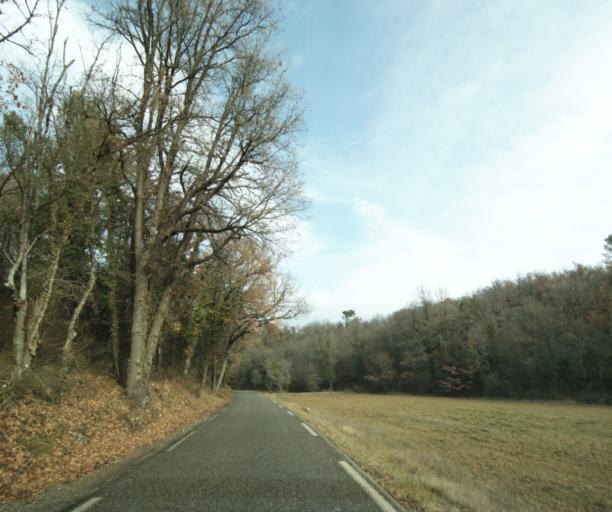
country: FR
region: Provence-Alpes-Cote d'Azur
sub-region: Departement du Var
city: Rougiers
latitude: 43.4160
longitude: 5.8699
